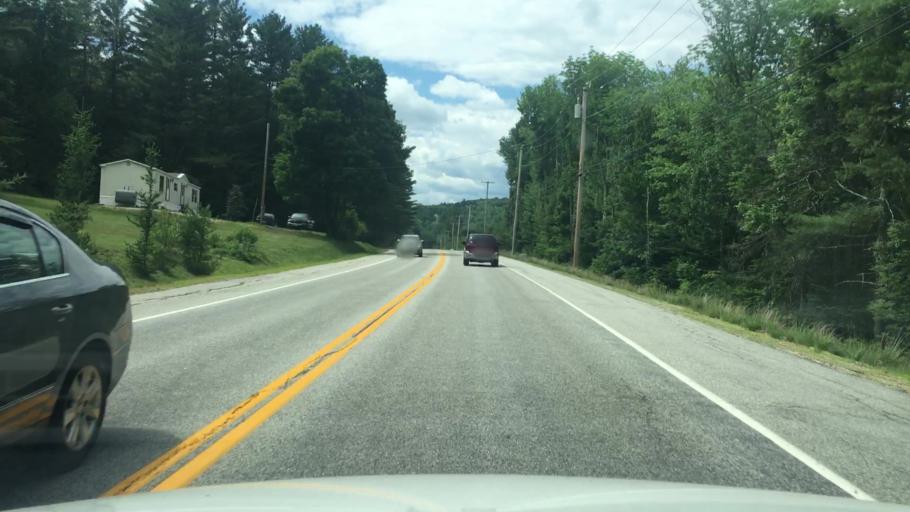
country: US
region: Maine
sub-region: Oxford County
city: West Paris
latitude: 44.3827
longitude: -70.6214
